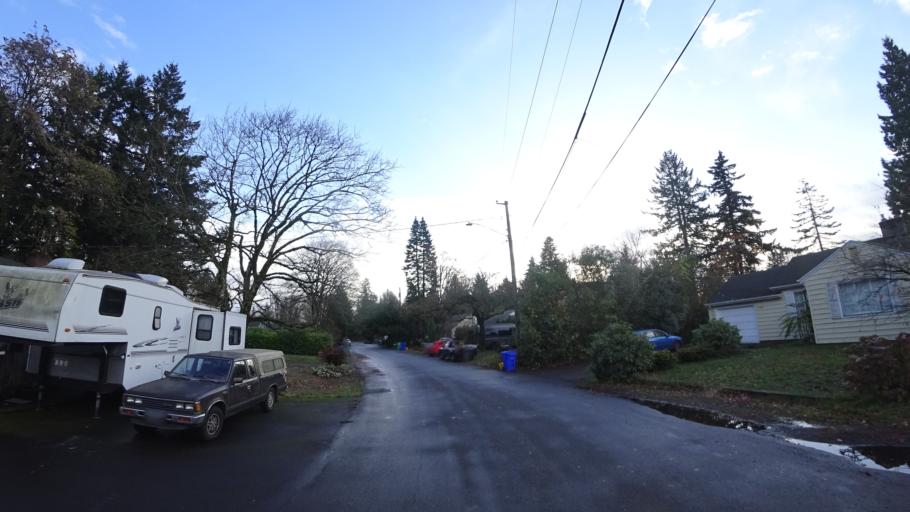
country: US
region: Oregon
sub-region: Multnomah County
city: Lents
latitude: 45.5214
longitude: -122.5480
